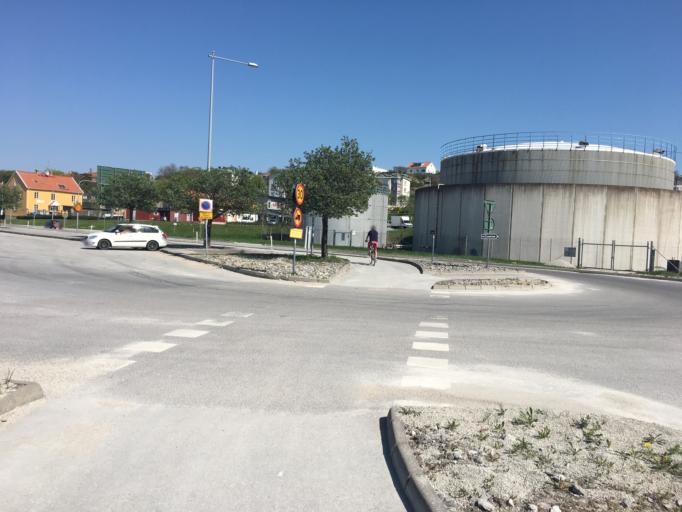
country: SE
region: Gotland
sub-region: Gotland
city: Visby
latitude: 57.6315
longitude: 18.2773
